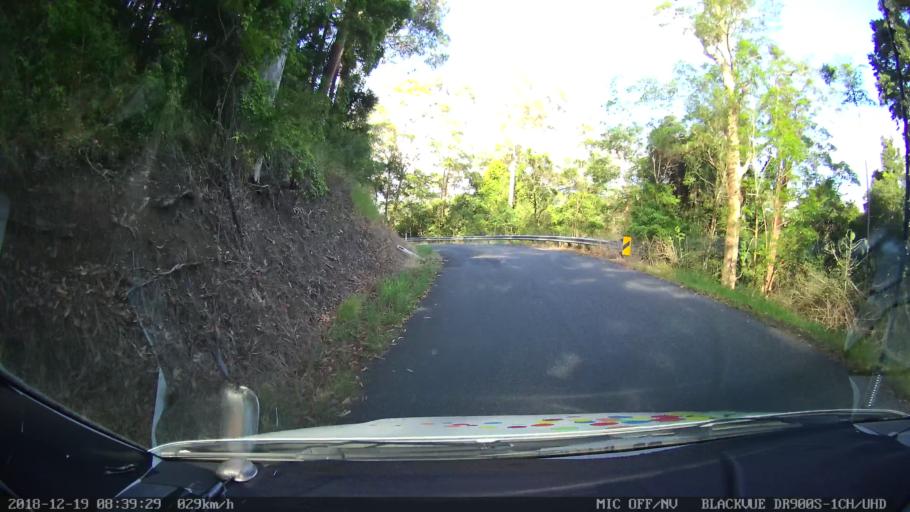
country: AU
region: New South Wales
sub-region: Kyogle
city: Kyogle
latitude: -28.3365
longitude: 152.9716
